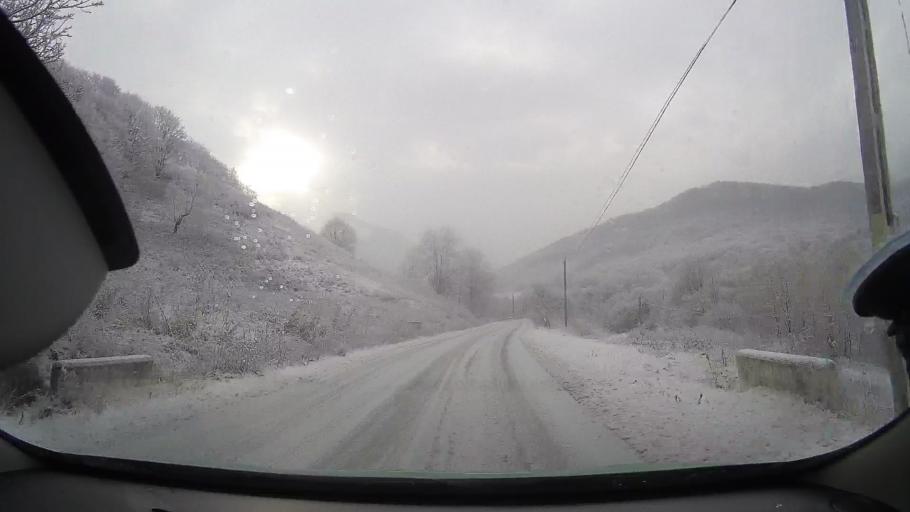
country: RO
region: Alba
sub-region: Comuna Rimetea
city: Rimetea
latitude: 46.4813
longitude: 23.5807
